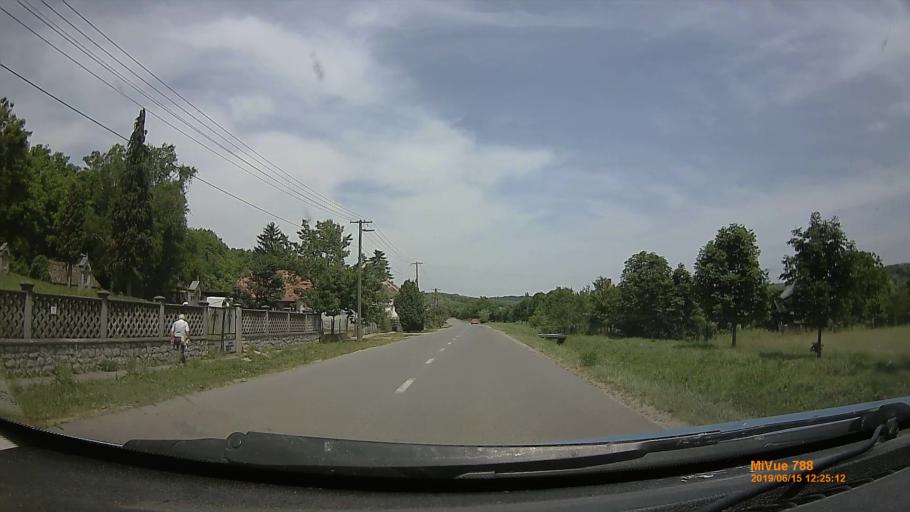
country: HU
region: Baranya
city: Buekkoesd
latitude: 46.1131
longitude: 17.9954
